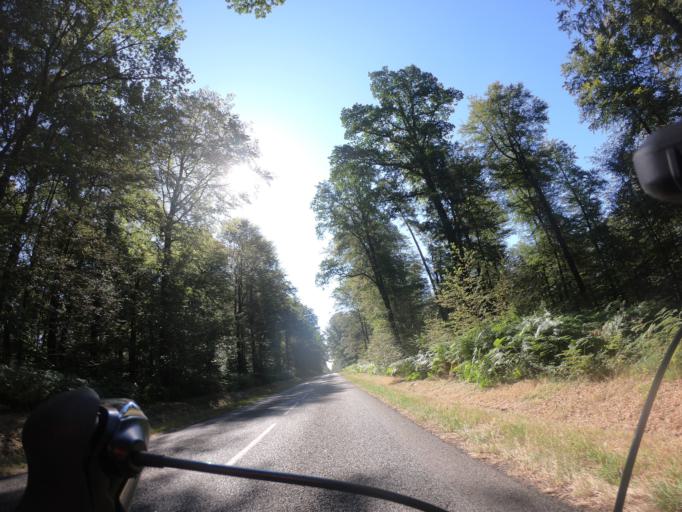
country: FR
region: Lower Normandy
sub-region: Departement de l'Orne
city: Tesse-la-Madeleine
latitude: 48.5739
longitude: -0.4566
